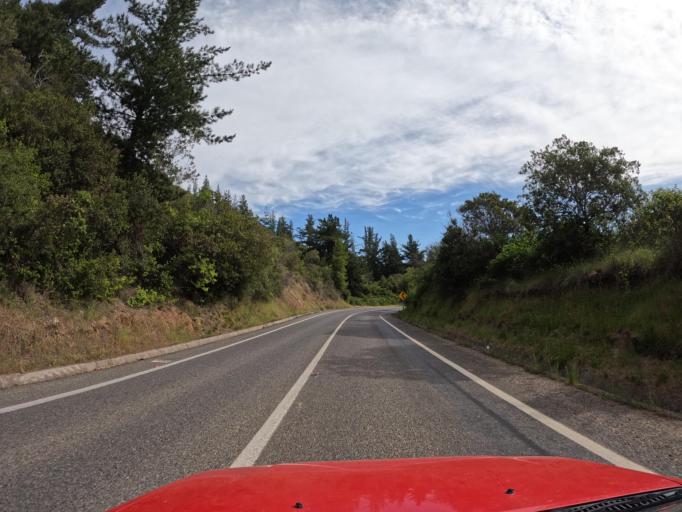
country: CL
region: Maule
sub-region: Provincia de Talca
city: Talca
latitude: -35.3010
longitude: -71.9618
